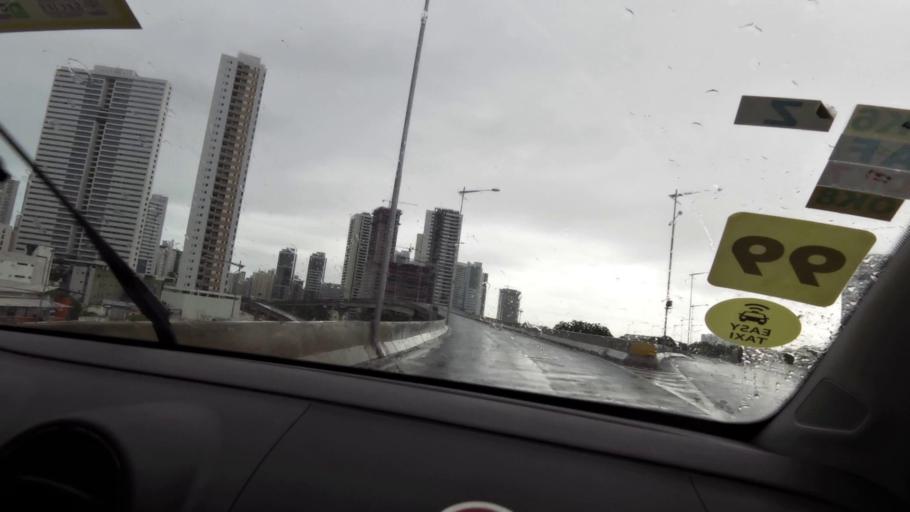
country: BR
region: Pernambuco
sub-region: Recife
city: Recife
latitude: -8.1252
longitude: -34.9017
